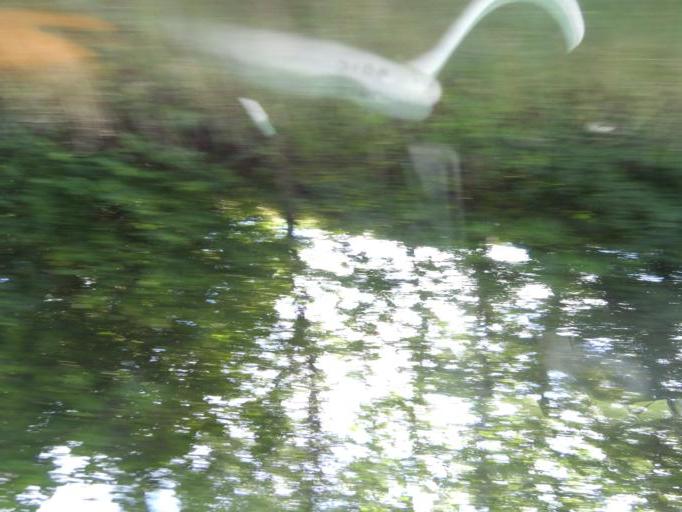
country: DK
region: South Denmark
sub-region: Assens Kommune
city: Vissenbjerg
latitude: 55.3957
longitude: 10.1499
